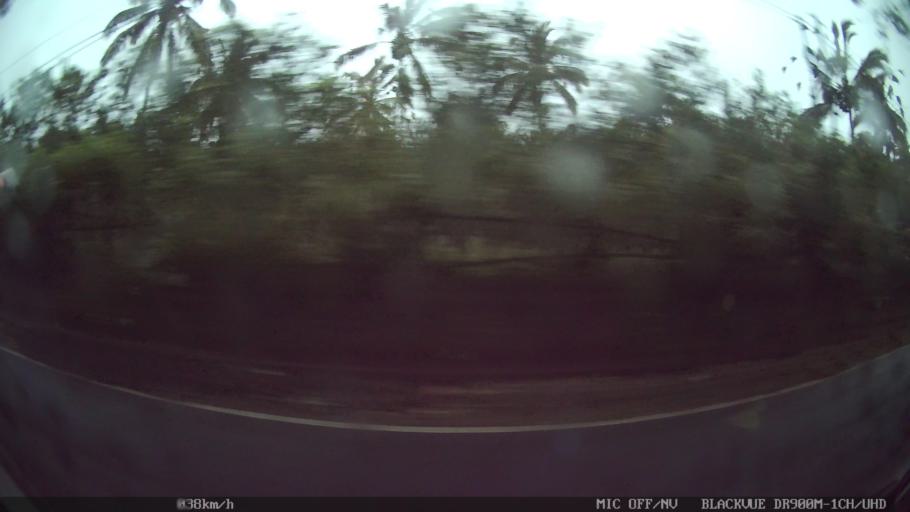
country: ID
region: Bali
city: Banjar Taro Kelod
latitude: -8.3679
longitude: 115.2701
